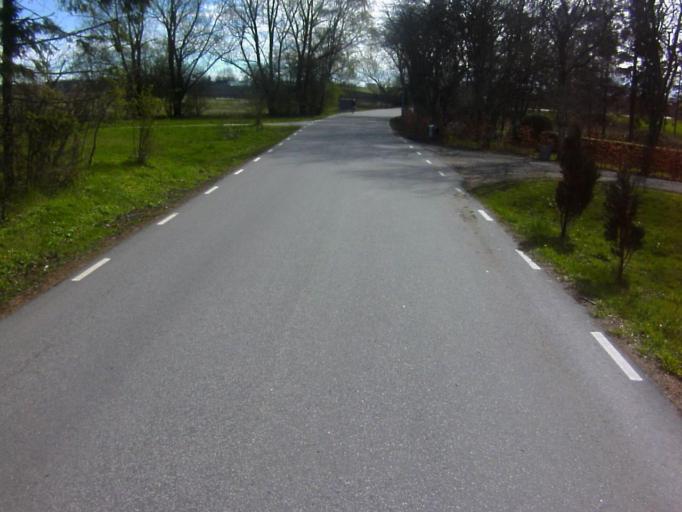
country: SE
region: Skane
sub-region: Kavlinge Kommun
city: Hofterup
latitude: 55.7901
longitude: 12.9686
